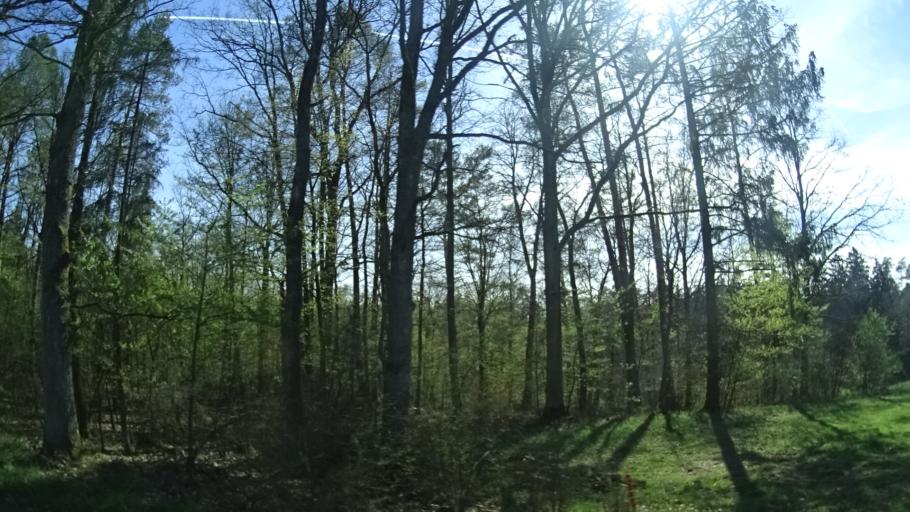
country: DE
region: Bavaria
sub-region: Regierungsbezirk Unterfranken
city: Burgpreppach
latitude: 50.1308
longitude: 10.6133
